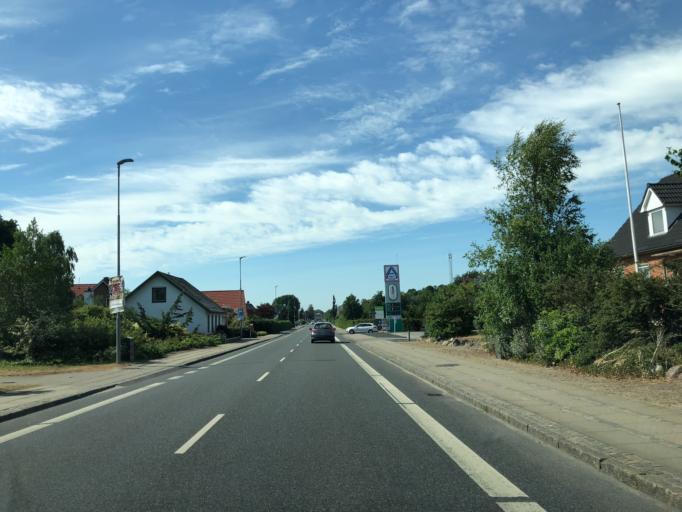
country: DK
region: Central Jutland
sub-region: Ikast-Brande Kommune
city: Brande
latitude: 55.9374
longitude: 9.1361
